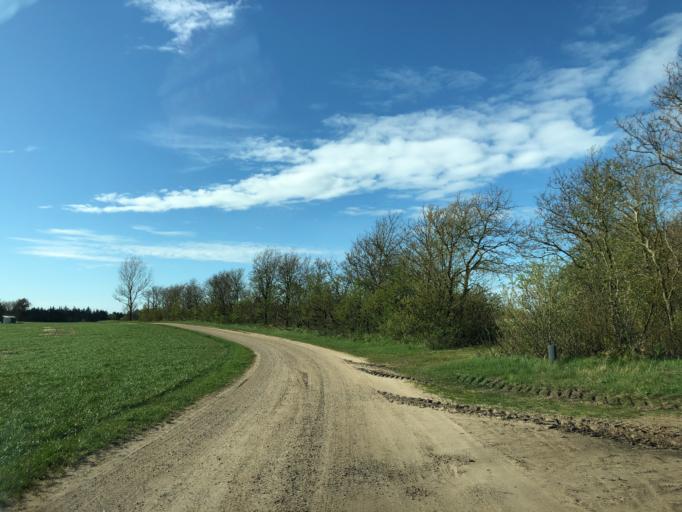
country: DK
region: Central Jutland
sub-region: Holstebro Kommune
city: Ulfborg
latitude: 56.2510
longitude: 8.3300
